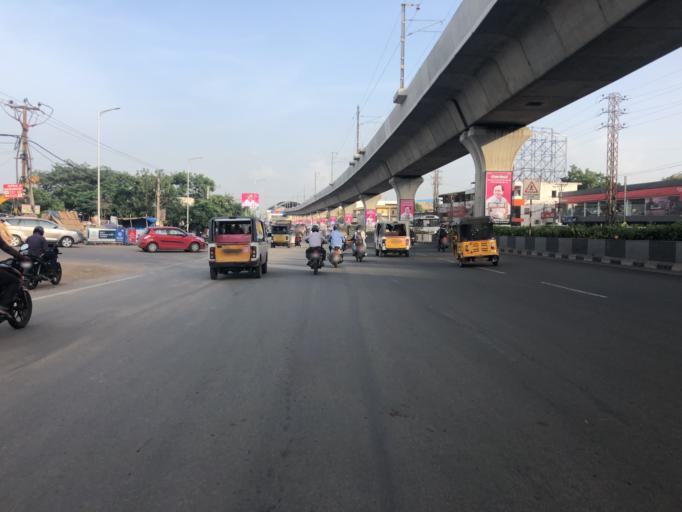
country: IN
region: Telangana
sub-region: Rangareddi
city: Kukatpalli
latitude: 17.4798
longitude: 78.4181
